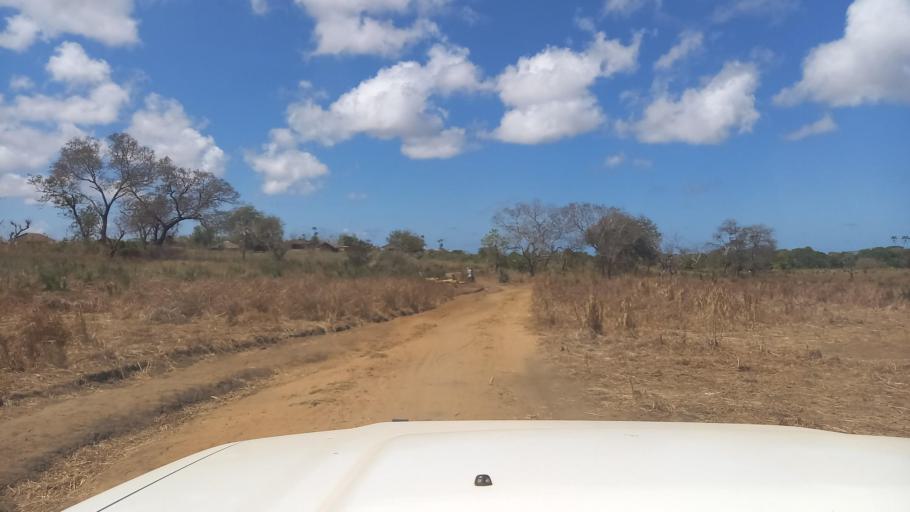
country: MZ
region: Cabo Delgado
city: Pemba
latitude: -13.4227
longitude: 40.4772
